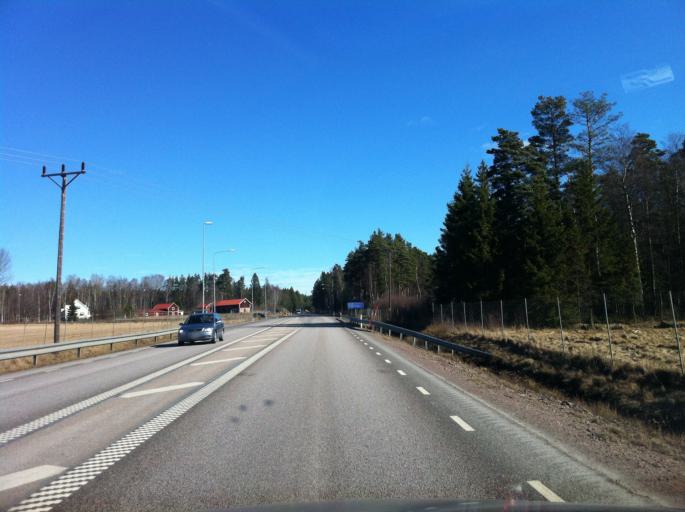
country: SE
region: Vaestra Goetaland
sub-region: Tibro Kommun
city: Tibro
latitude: 58.4324
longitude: 14.1605
